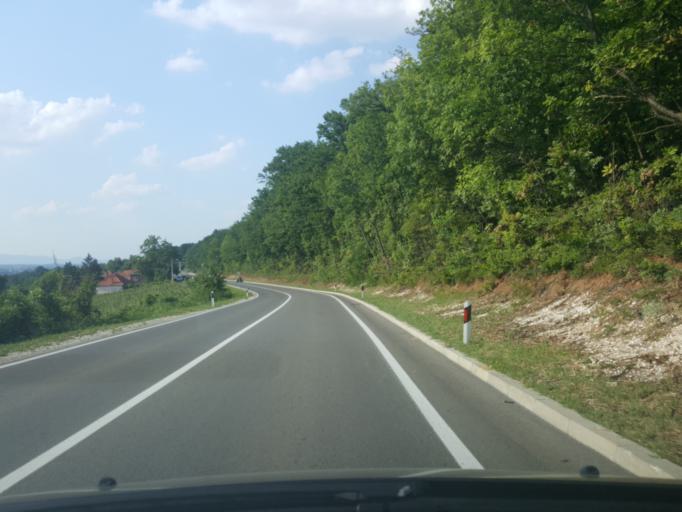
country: RS
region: Central Serbia
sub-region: Sumadijski Okrug
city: Topola
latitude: 44.2357
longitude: 20.6781
